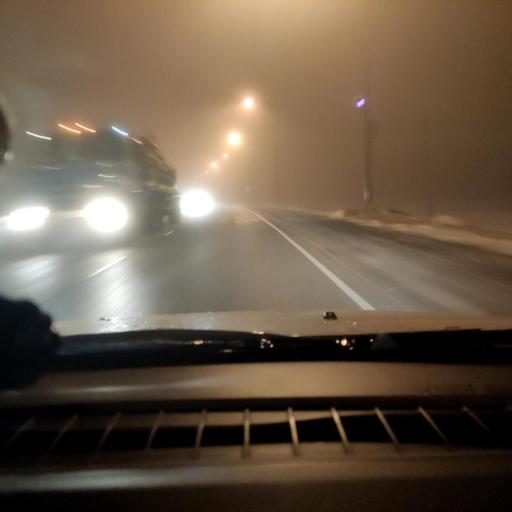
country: RU
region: Samara
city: Dubovyy Umet
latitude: 52.9667
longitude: 50.2820
